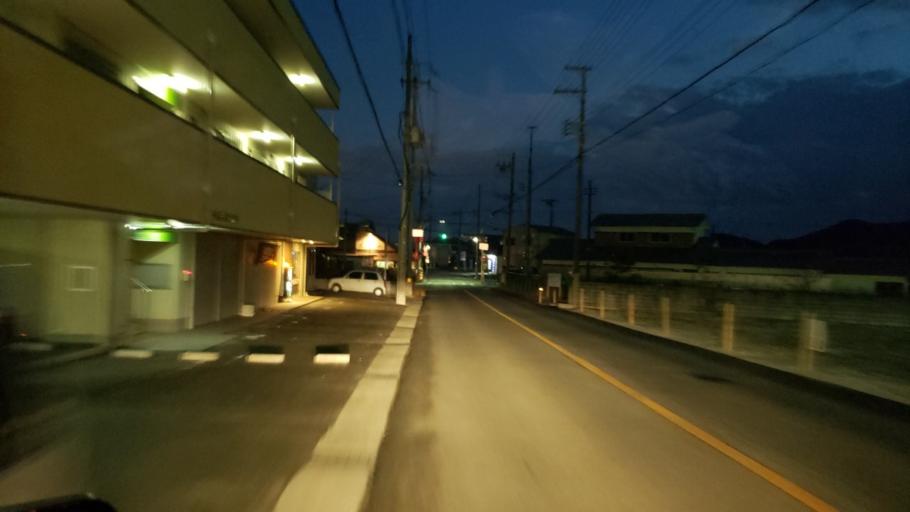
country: JP
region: Hyogo
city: Kakogawacho-honmachi
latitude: 34.8150
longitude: 134.8186
